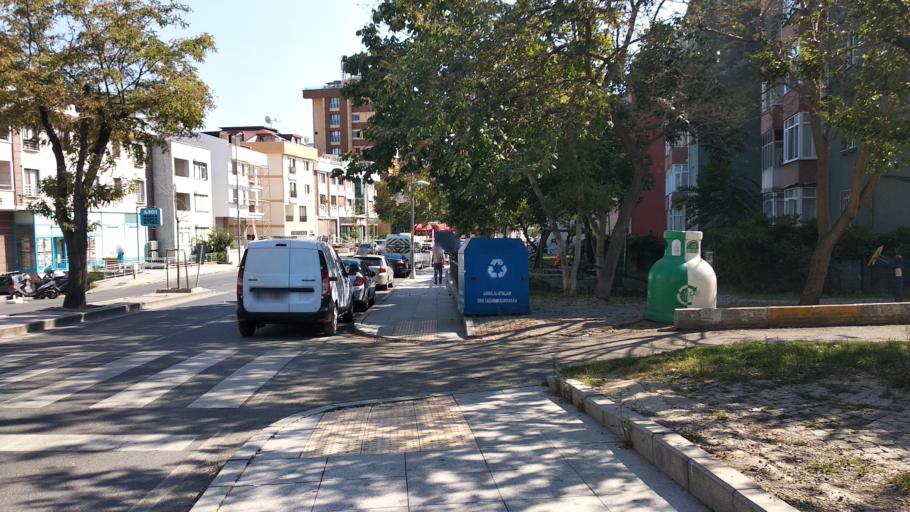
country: TR
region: Istanbul
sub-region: Atasehir
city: Atasehir
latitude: 40.9973
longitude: 29.0819
